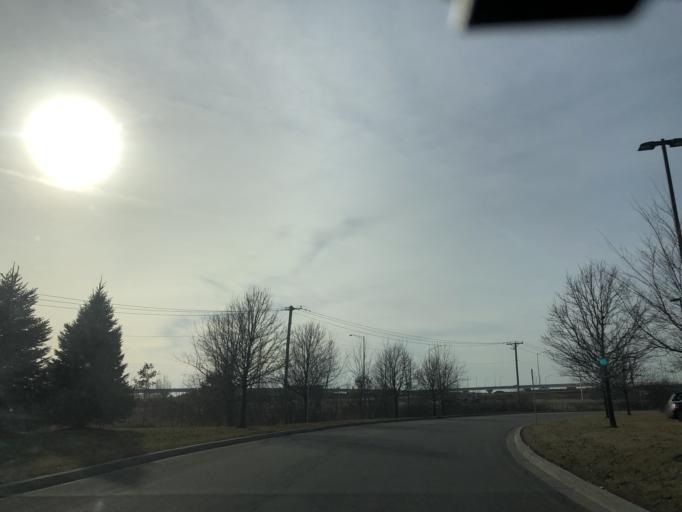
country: US
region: Illinois
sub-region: Cook County
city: Lemont
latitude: 41.7085
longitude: -88.0259
